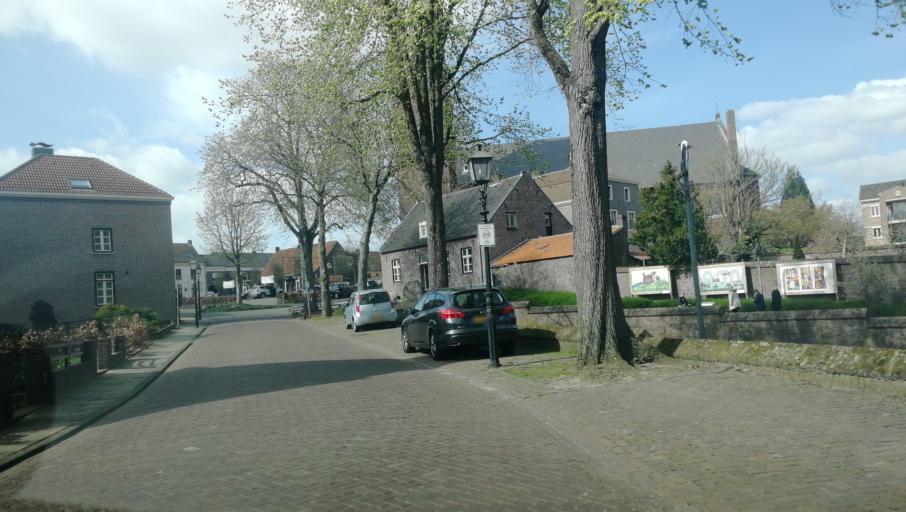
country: NL
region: Limburg
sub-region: Gemeente Venlo
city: Tegelen
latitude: 51.3304
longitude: 6.0976
